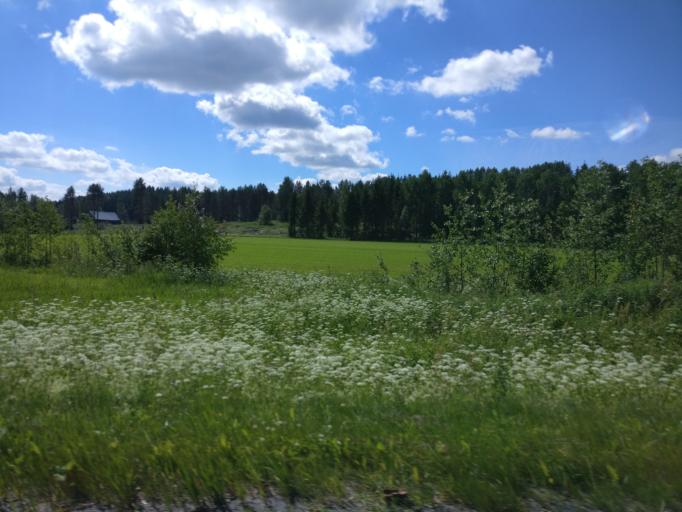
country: FI
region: Southern Savonia
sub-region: Savonlinna
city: Kerimaeki
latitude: 61.8839
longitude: 29.0970
